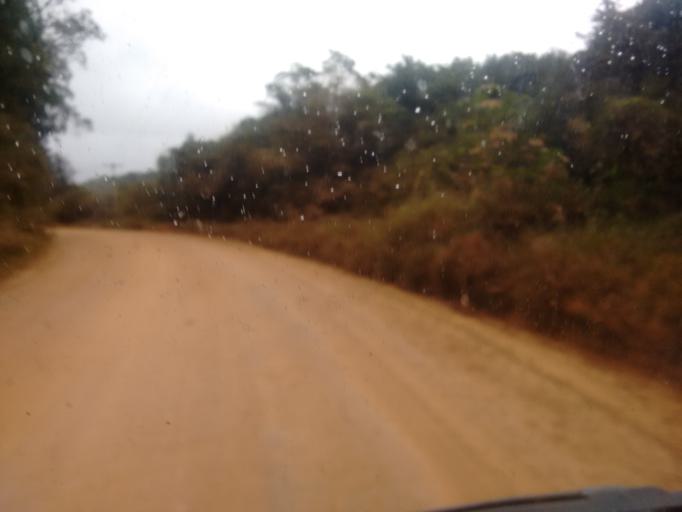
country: BR
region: Rio Grande do Sul
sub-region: Camaqua
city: Camaqua
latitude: -30.8167
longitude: -51.8133
